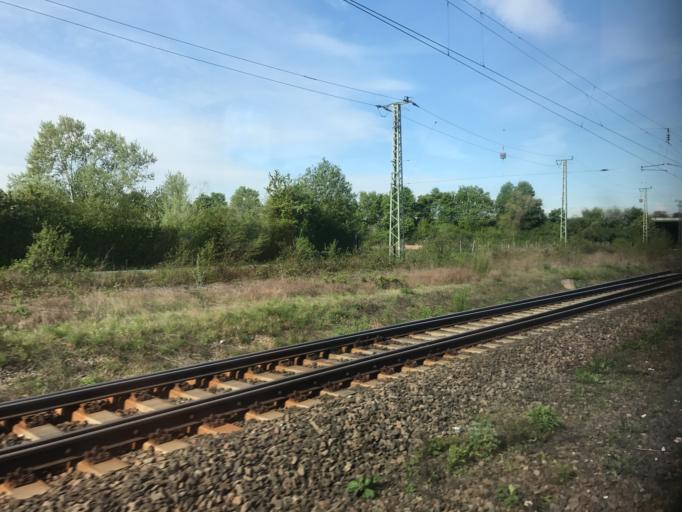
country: DE
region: Baden-Wuerttemberg
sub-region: Karlsruhe Region
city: Eppelheim
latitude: 49.4138
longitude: 8.6369
